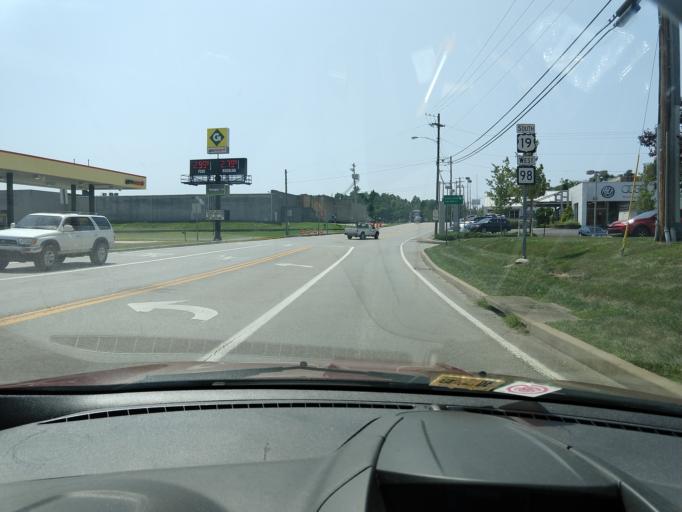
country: US
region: West Virginia
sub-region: Harrison County
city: Clarksburg
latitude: 39.2730
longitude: -80.3690
